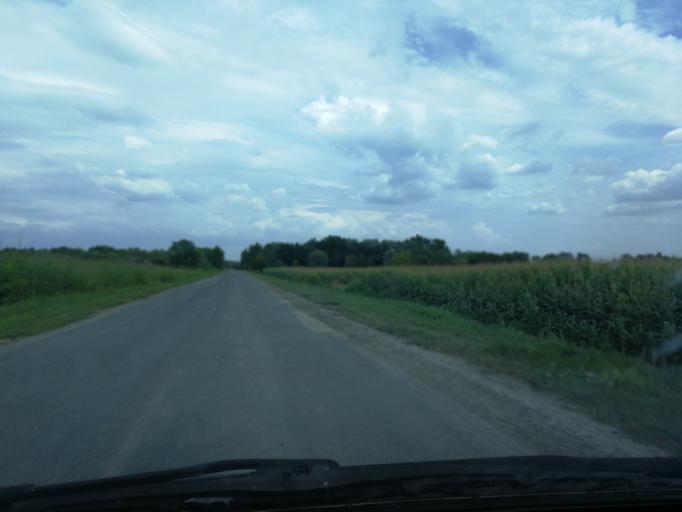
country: HU
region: Bacs-Kiskun
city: Dusnok
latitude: 46.4427
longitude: 18.9999
